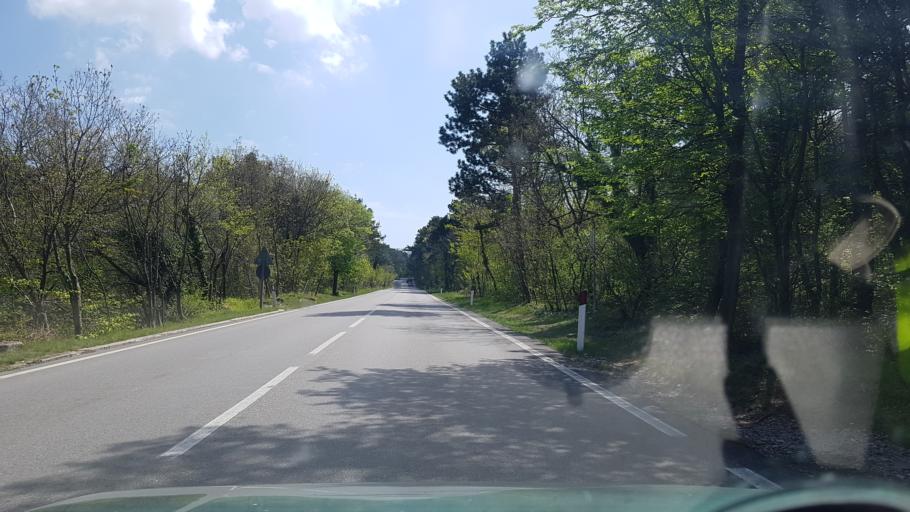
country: IT
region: Friuli Venezia Giulia
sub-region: Provincia di Trieste
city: Dolina
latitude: 45.6362
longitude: 13.8753
